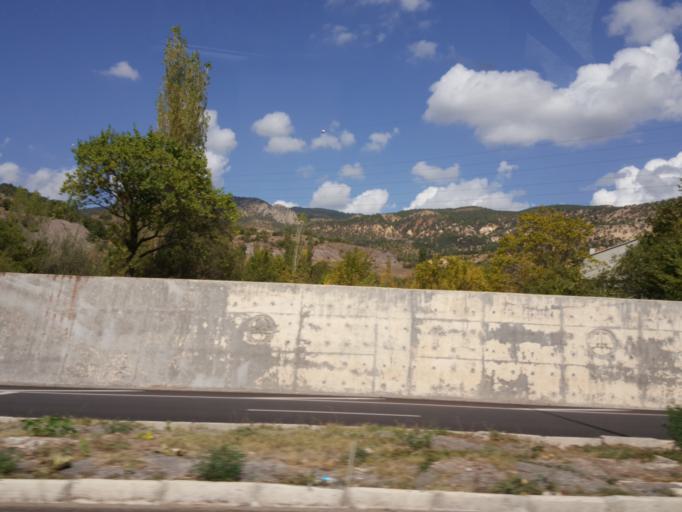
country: TR
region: Sivas
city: Koyulhisar
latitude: 40.2882
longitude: 37.7905
